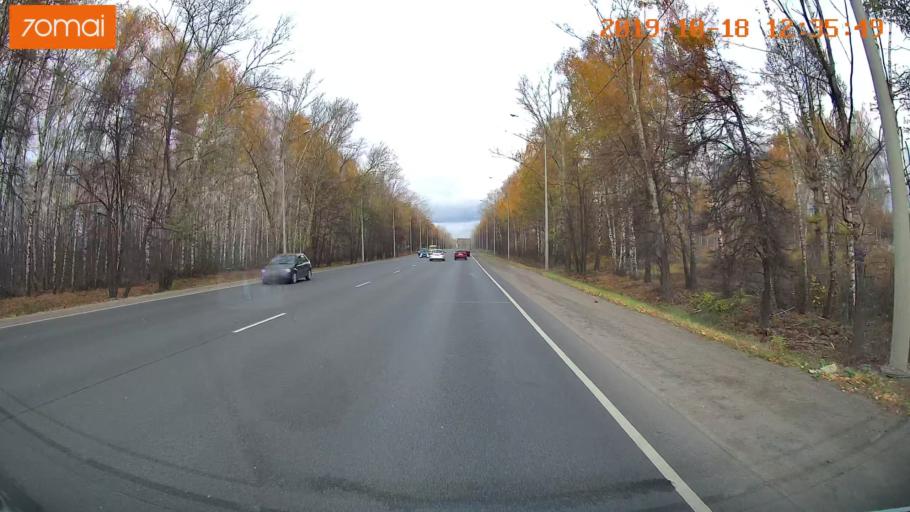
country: RU
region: Rjazan
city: Ryazan'
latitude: 54.6284
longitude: 39.6350
